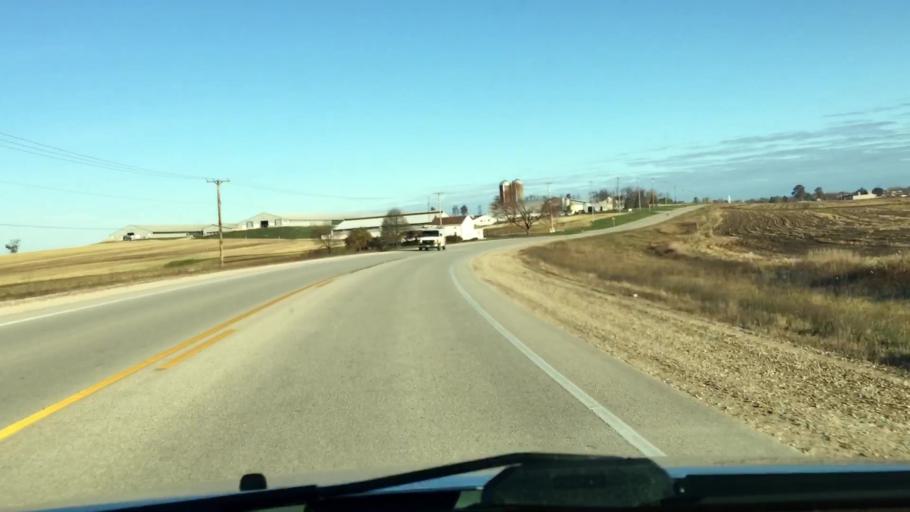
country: US
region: Wisconsin
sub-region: Dodge County
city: Lomira
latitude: 43.5689
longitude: -88.4495
